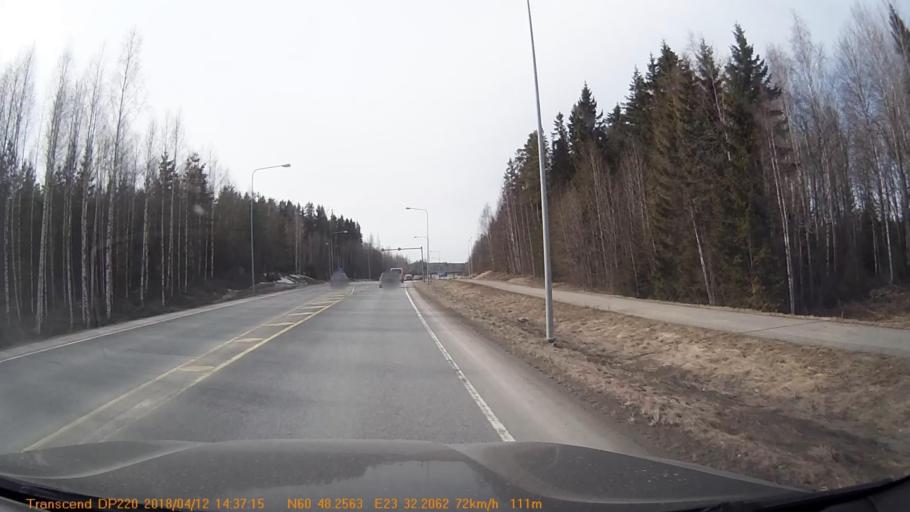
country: FI
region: Haeme
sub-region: Forssa
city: Jokioinen
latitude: 60.8048
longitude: 23.5344
